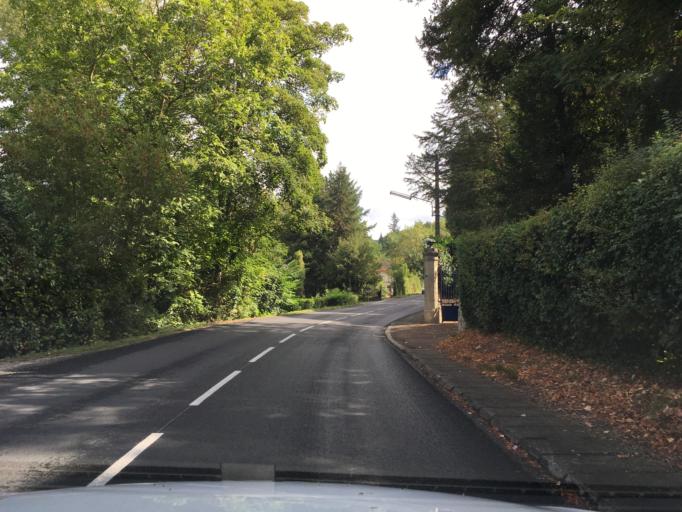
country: FR
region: Aquitaine
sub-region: Departement du Lot-et-Garonne
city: Le Passage
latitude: 44.2180
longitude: 0.6101
